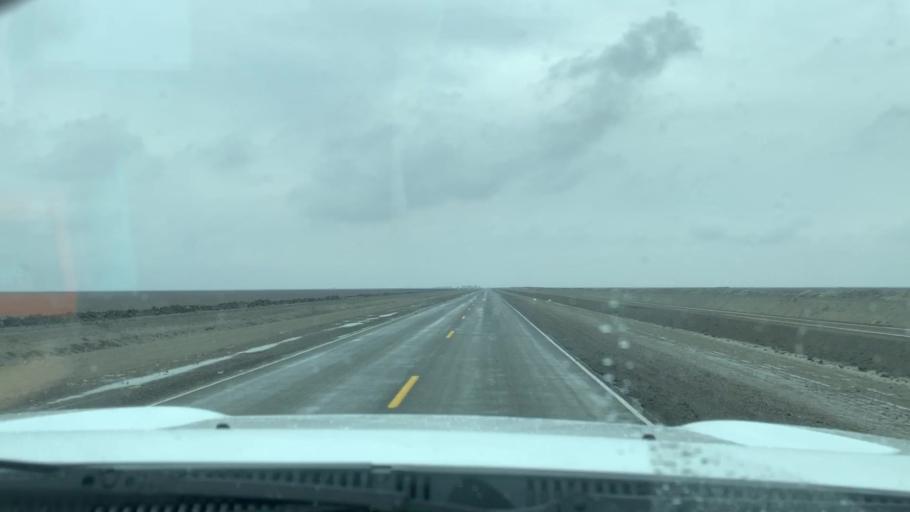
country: US
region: California
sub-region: Tulare County
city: Alpaugh
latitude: 35.9343
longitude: -119.6018
